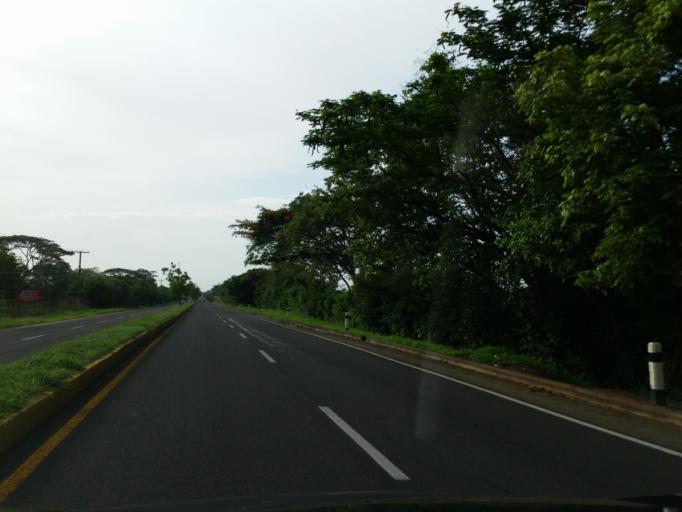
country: NI
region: Granada
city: Granada
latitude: 11.9475
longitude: -85.9827
